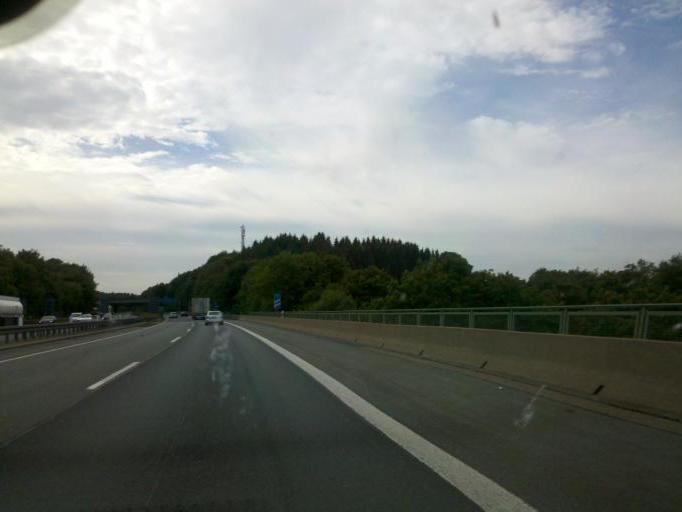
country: DE
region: North Rhine-Westphalia
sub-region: Regierungsbezirk Arnsberg
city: Luedenscheid
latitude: 51.2299
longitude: 7.6631
